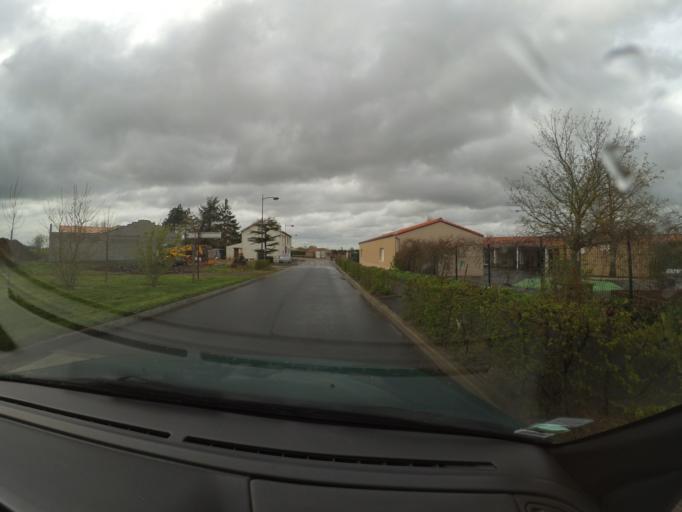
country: FR
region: Pays de la Loire
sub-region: Departement de la Loire-Atlantique
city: Monnieres
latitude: 47.1294
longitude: -1.3521
